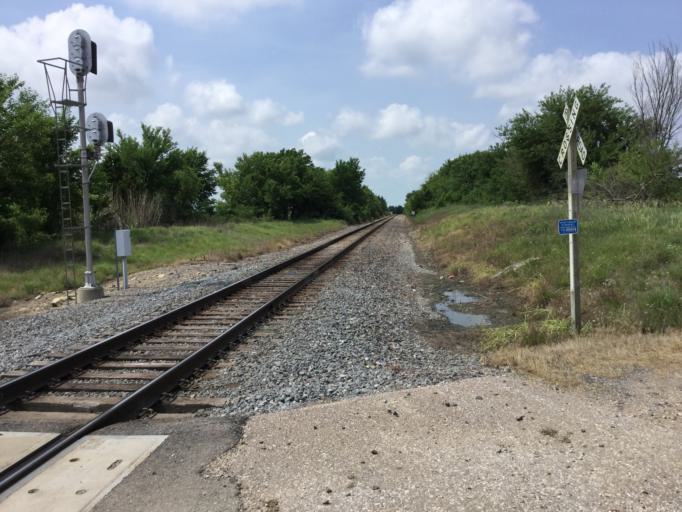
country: US
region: Kansas
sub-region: Anderson County
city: Garnett
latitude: 38.2271
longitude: -95.2935
